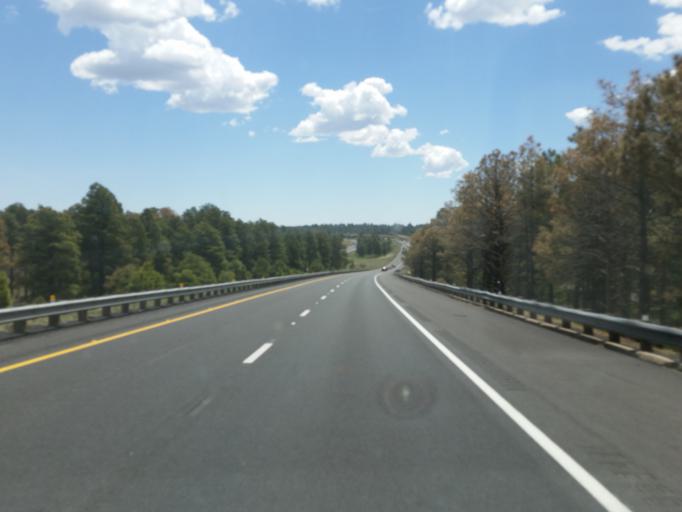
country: US
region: Arizona
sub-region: Coconino County
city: Flagstaff
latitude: 35.1764
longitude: -111.6751
